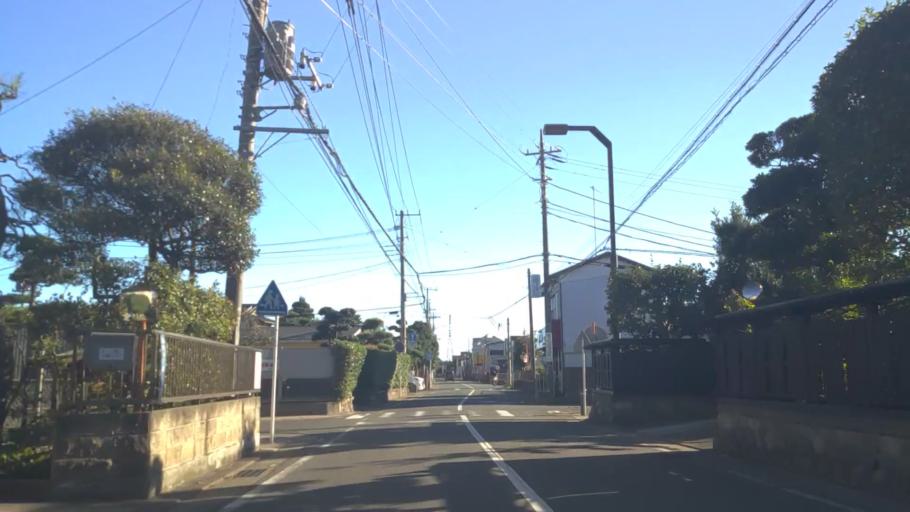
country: JP
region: Kanagawa
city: Isehara
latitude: 35.3790
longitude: 139.3649
